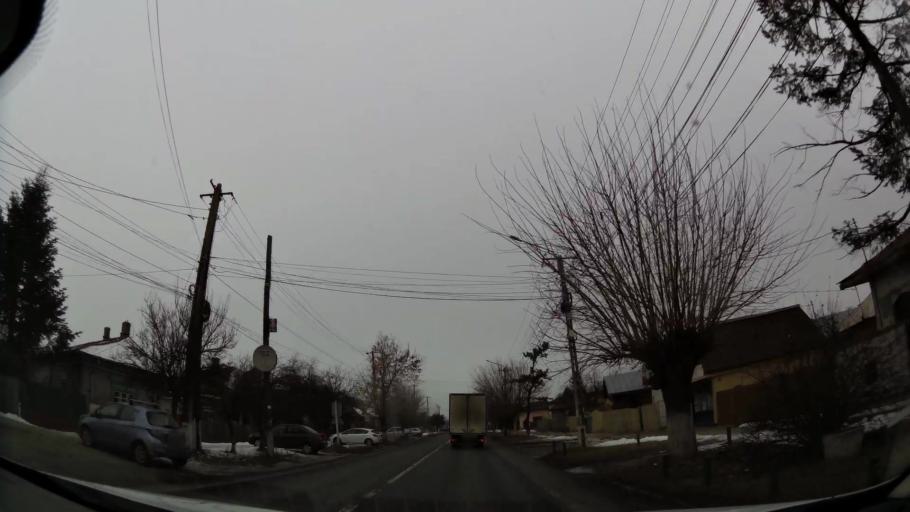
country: RO
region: Dambovita
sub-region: Comuna Racari
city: Racari
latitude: 44.6275
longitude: 25.7379
